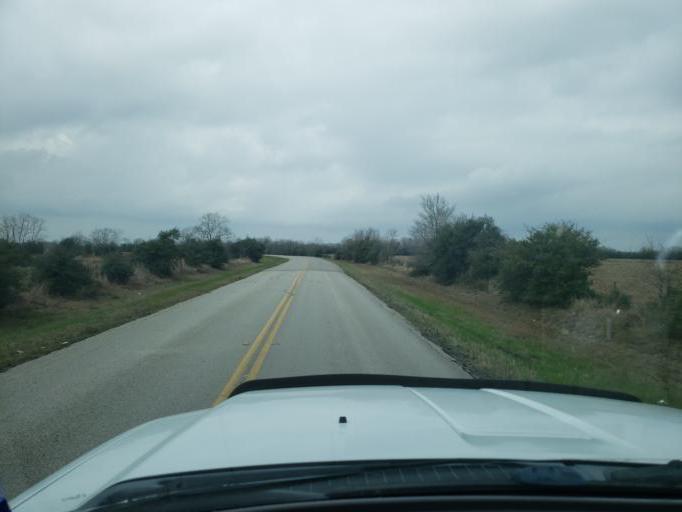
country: US
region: Texas
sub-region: Fort Bend County
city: Needville
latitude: 29.3692
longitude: -95.7284
